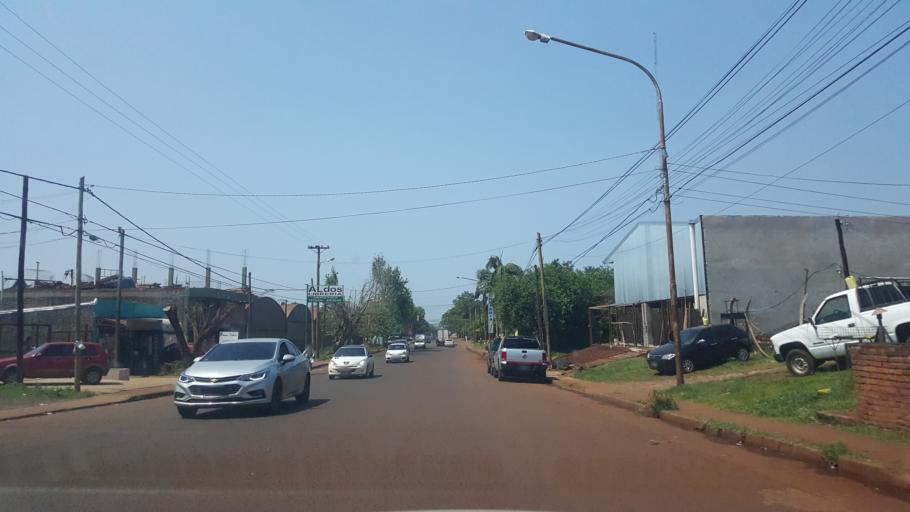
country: AR
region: Misiones
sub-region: Departamento de Capital
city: Posadas
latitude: -27.3863
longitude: -55.9132
